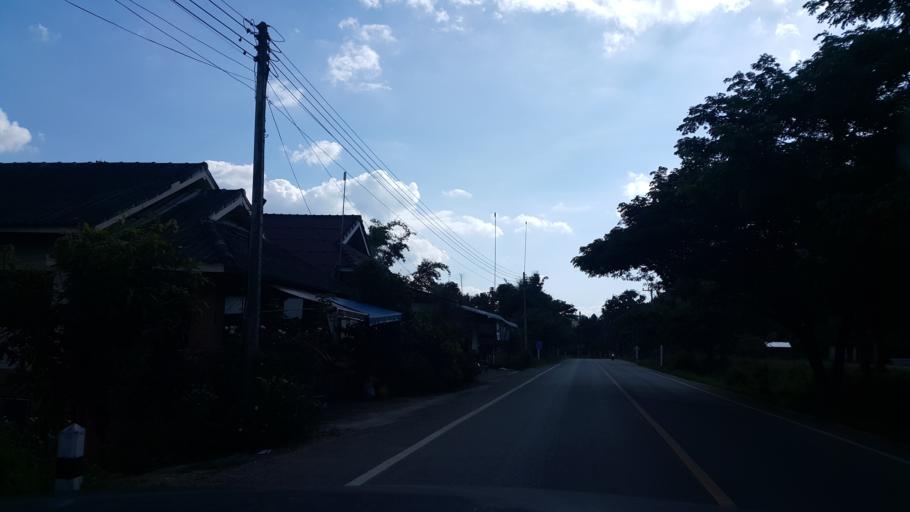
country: TH
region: Lamphun
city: Ban Thi
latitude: 18.5800
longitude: 99.2608
